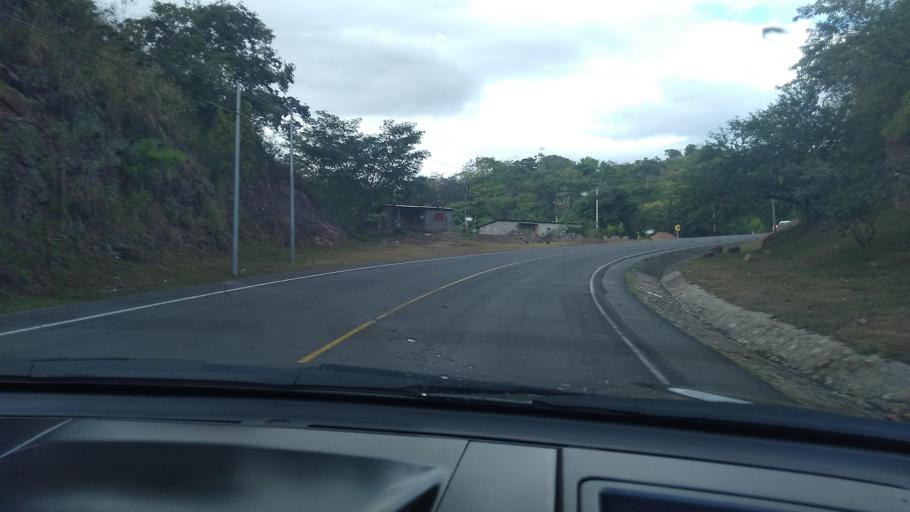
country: NI
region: Madriz
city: Yalaguina
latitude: 13.4945
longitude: -86.5021
